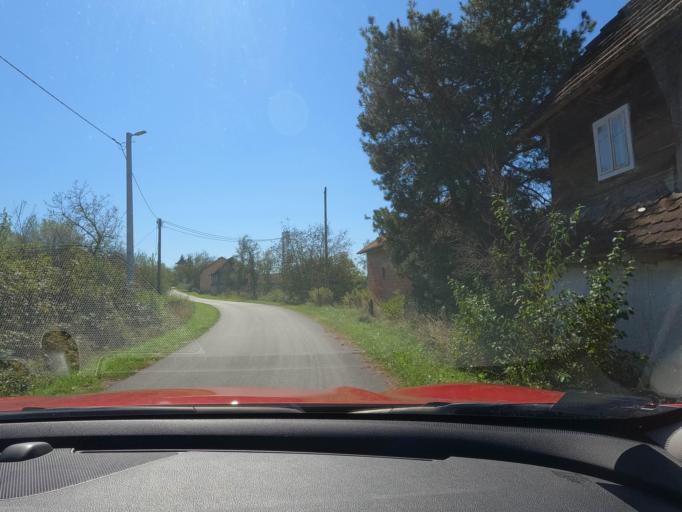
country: HR
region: Sisacko-Moslavacka
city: Petrinja
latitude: 45.3558
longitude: 16.2483
